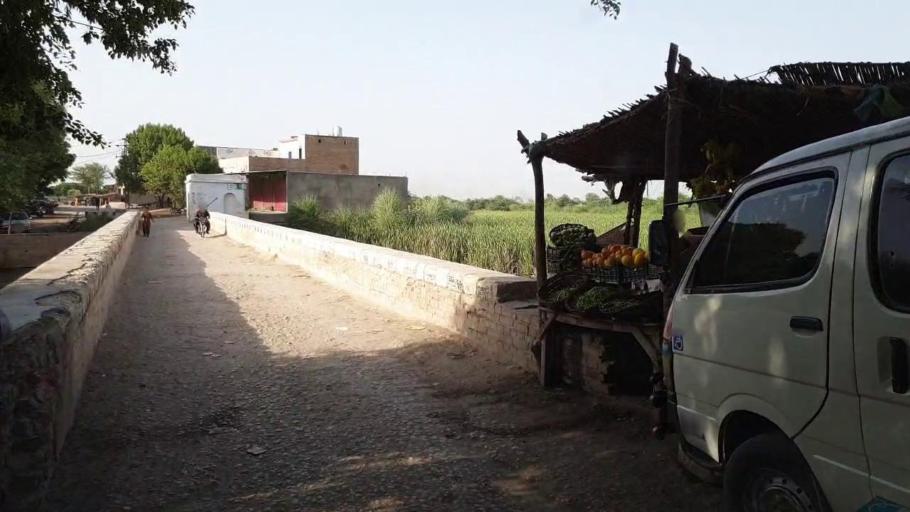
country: PK
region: Sindh
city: Jam Sahib
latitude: 26.4286
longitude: 68.8736
